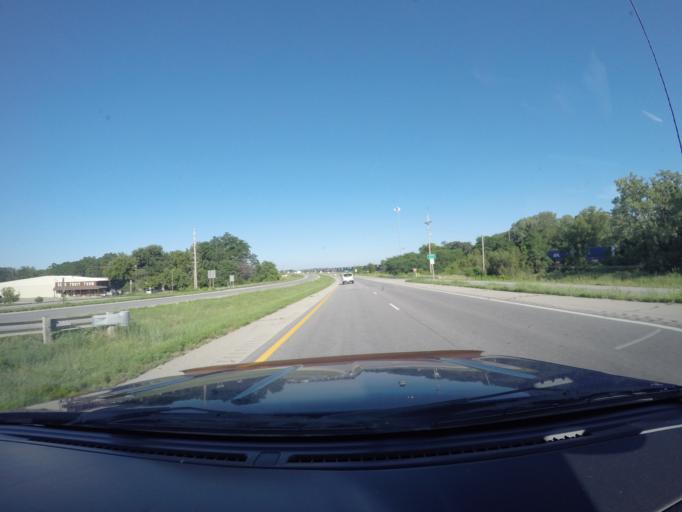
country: US
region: Kansas
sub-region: Shawnee County
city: Topeka
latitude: 39.0906
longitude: -95.5956
